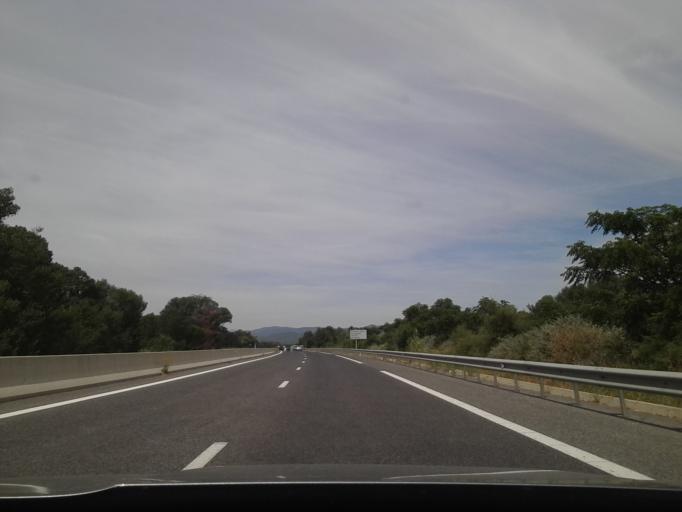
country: FR
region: Languedoc-Roussillon
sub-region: Departement des Pyrenees-Orientales
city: Corneilla-la-Riviere
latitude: 42.6892
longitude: 2.7275
